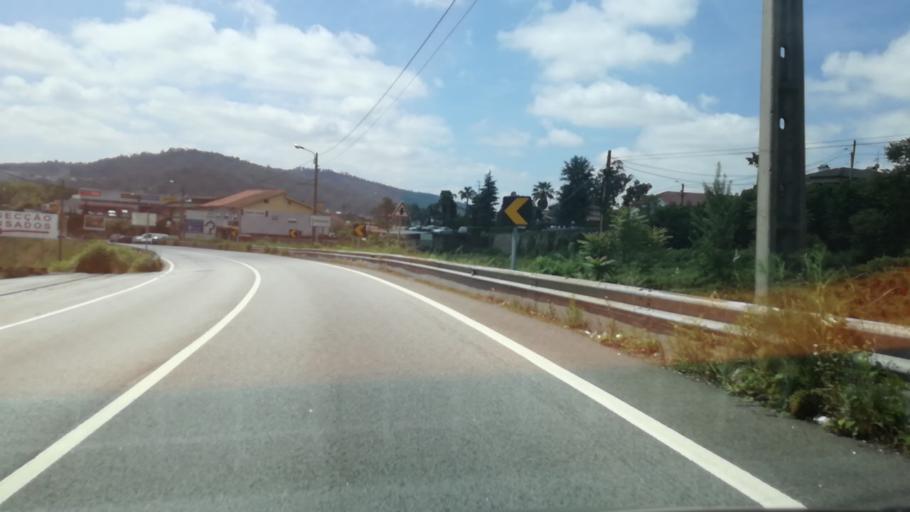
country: PT
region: Braga
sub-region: Braga
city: Braga
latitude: 41.5208
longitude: -8.4502
